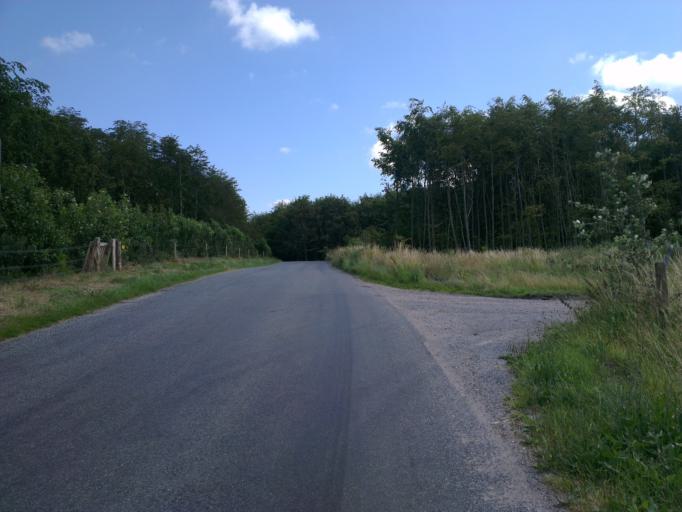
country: DK
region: Zealand
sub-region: Lejre Kommune
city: Ejby
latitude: 55.7543
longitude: 11.8496
